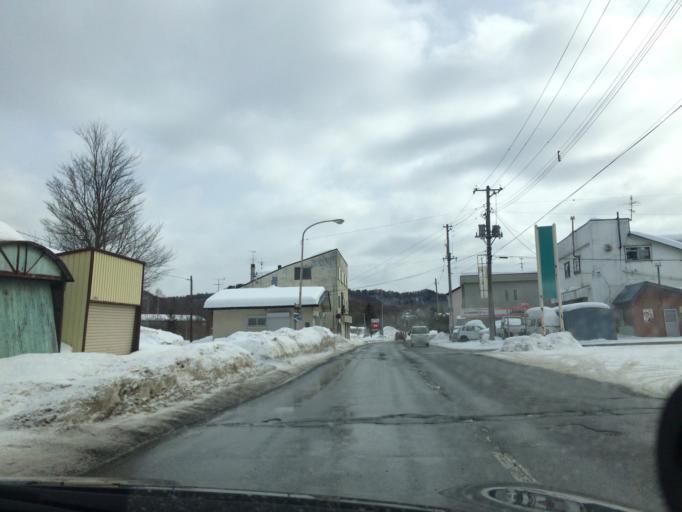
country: JP
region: Hokkaido
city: Iwamizawa
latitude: 42.9583
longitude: 142.0291
